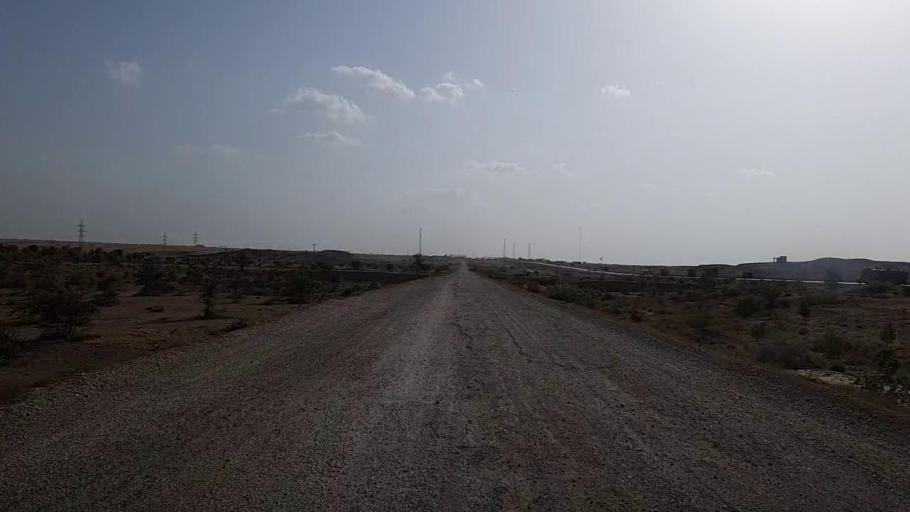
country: PK
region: Sindh
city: Kotri
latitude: 25.2606
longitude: 67.9799
